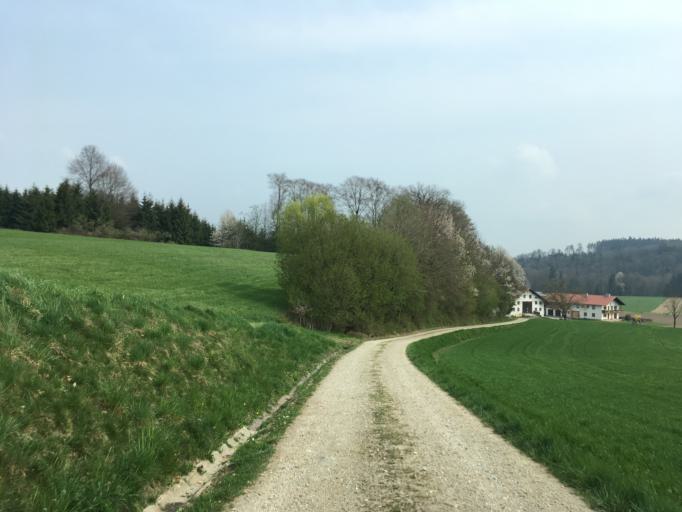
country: DE
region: Bavaria
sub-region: Upper Bavaria
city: Jettenbach
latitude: 48.1608
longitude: 12.3752
